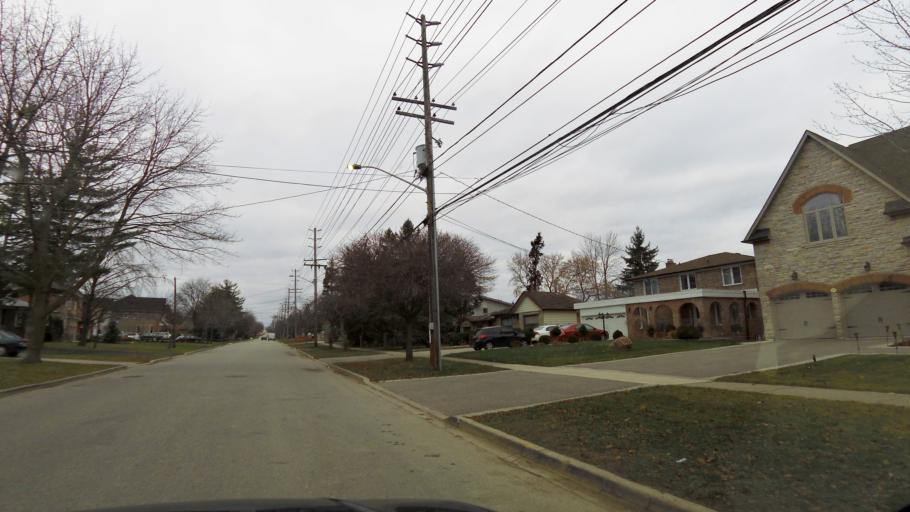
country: CA
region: Ontario
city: Mississauga
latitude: 43.5520
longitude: -79.6352
